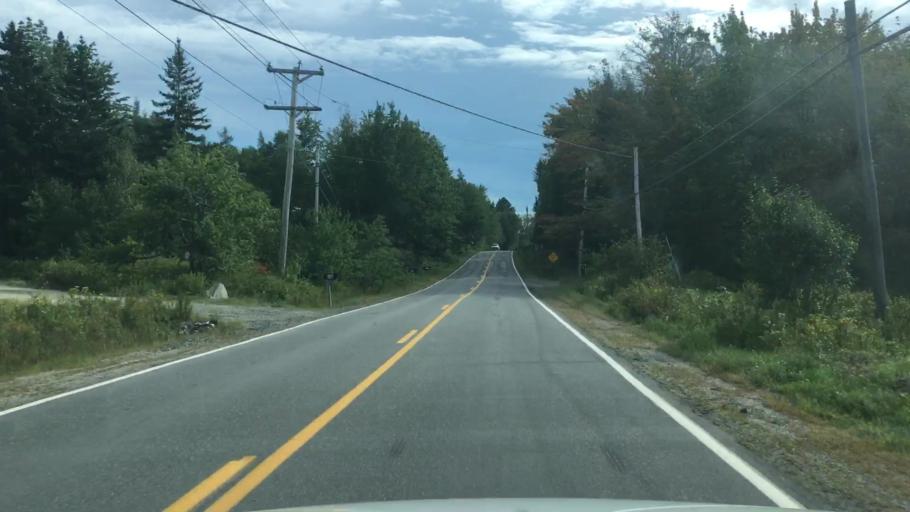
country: US
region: Maine
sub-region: Hancock County
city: Ellsworth
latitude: 44.4848
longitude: -68.4202
